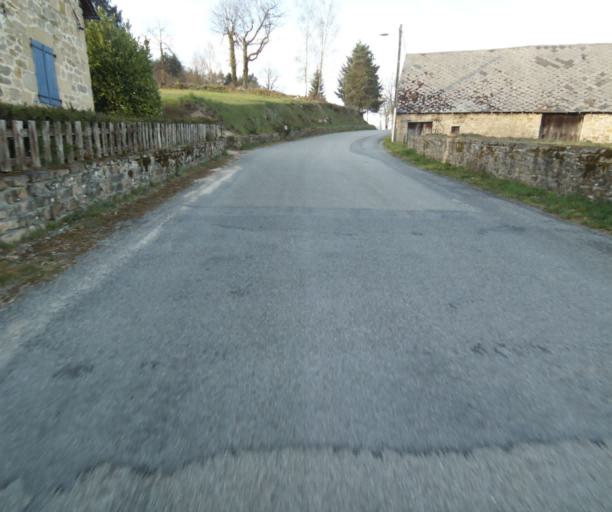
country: FR
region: Limousin
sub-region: Departement de la Correze
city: Correze
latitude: 45.3694
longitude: 1.8707
